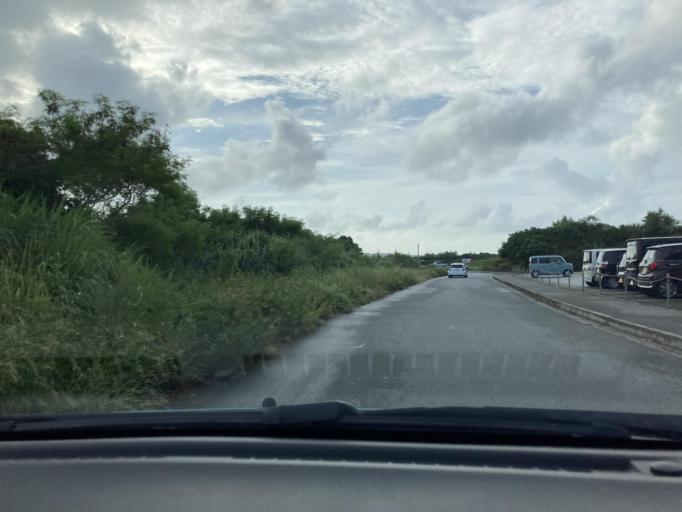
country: JP
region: Okinawa
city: Tomigusuku
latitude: 26.1756
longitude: 127.6427
